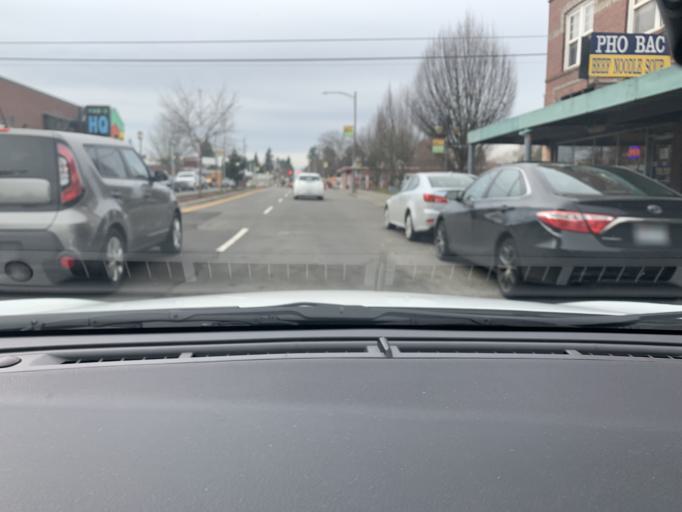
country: US
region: Washington
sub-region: Pierce County
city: Tacoma
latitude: 47.2521
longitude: -122.4522
